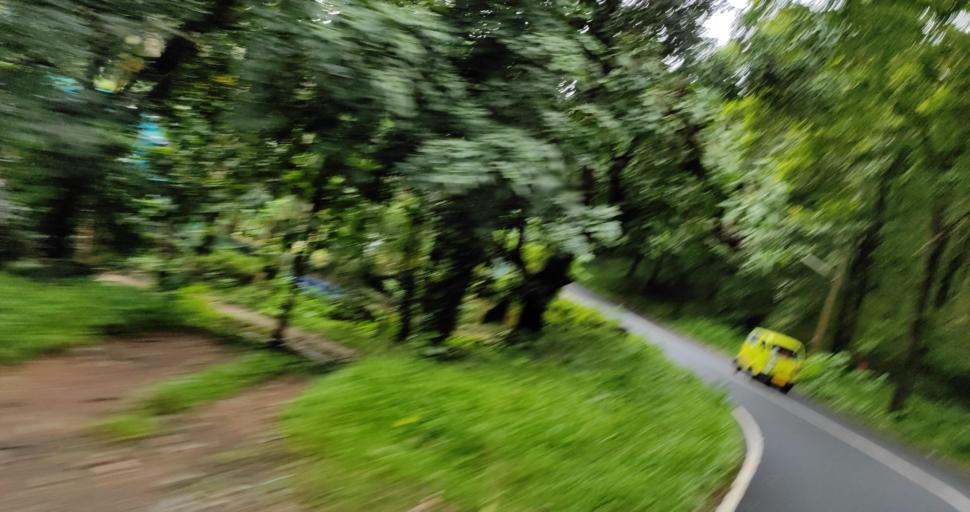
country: IN
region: Kerala
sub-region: Thrissur District
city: Kizhake Chalakudi
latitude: 10.3009
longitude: 76.4440
